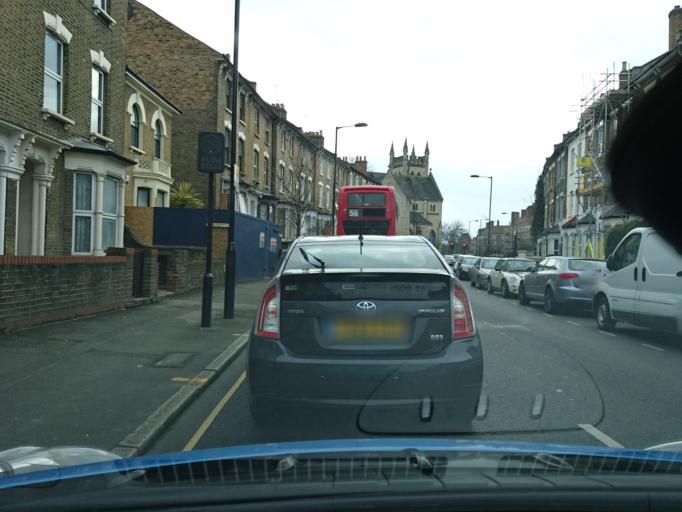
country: GB
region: England
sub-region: Greater London
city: Hackney
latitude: 51.5538
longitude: -0.0570
